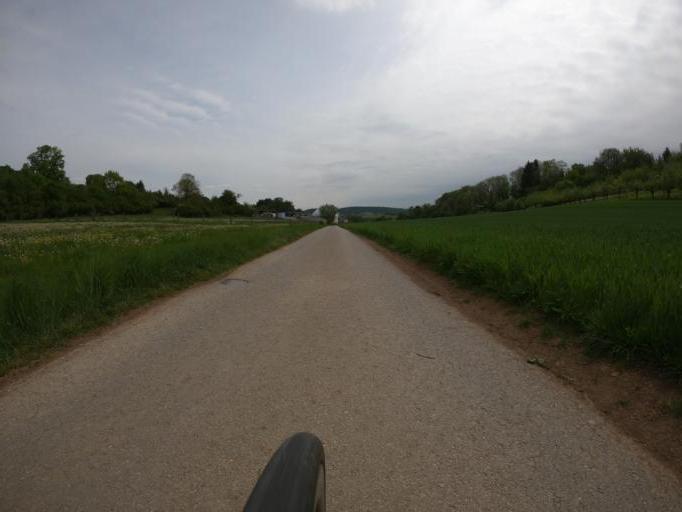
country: DE
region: Baden-Wuerttemberg
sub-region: Regierungsbezirk Stuttgart
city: Aidlingen
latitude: 48.6867
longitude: 8.8823
